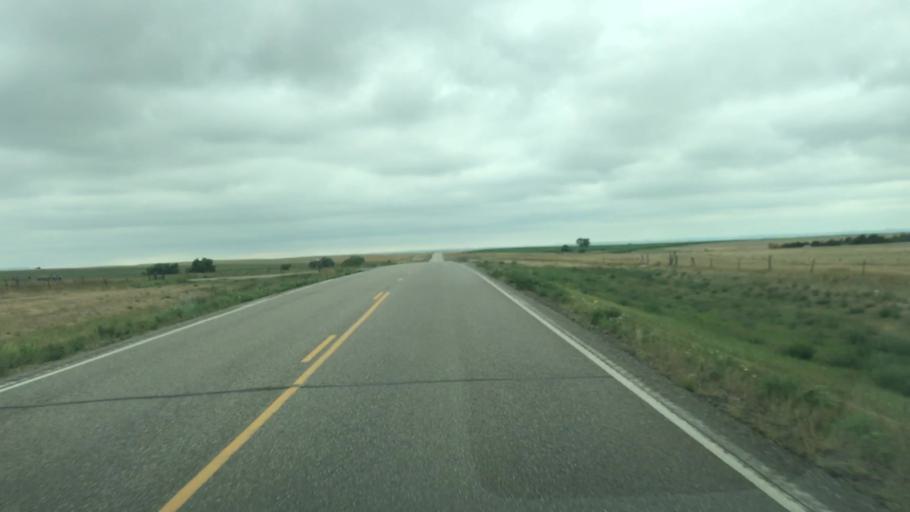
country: US
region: South Dakota
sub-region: Jackson County
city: Kadoka
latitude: 43.8201
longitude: -101.5224
